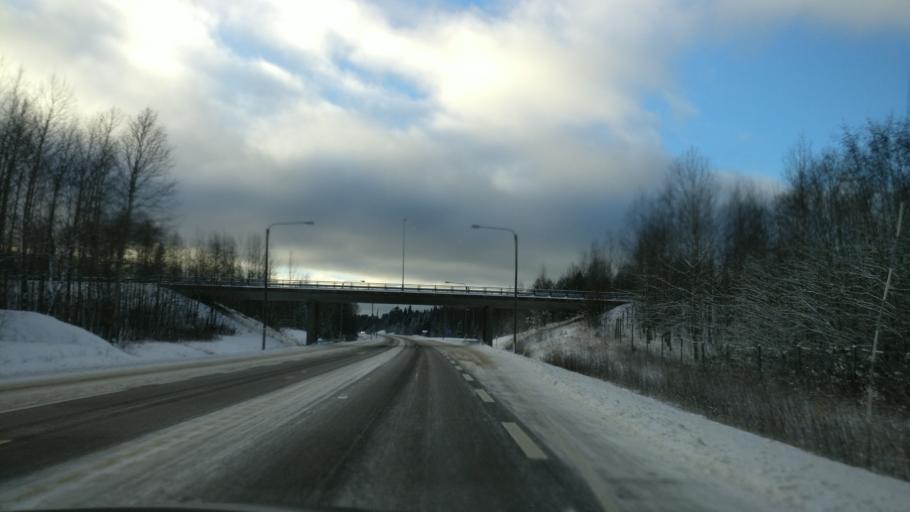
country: FI
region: Southern Savonia
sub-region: Mikkeli
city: Pertunmaa
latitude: 61.3657
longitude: 26.2577
